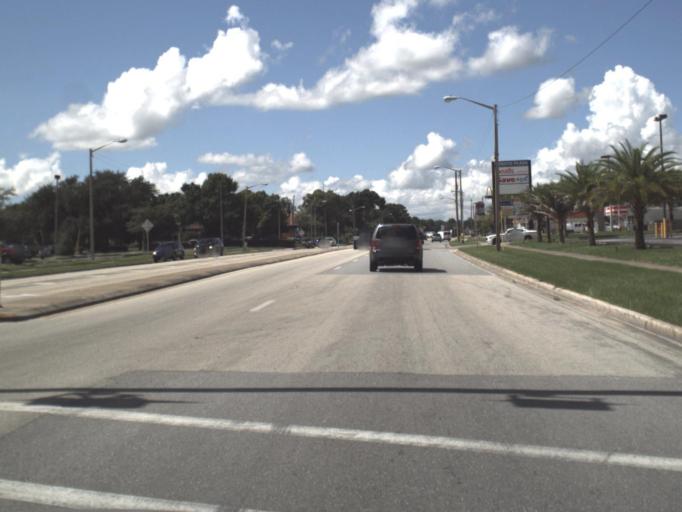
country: US
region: Florida
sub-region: DeSoto County
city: Arcadia
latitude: 27.2097
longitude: -81.8430
